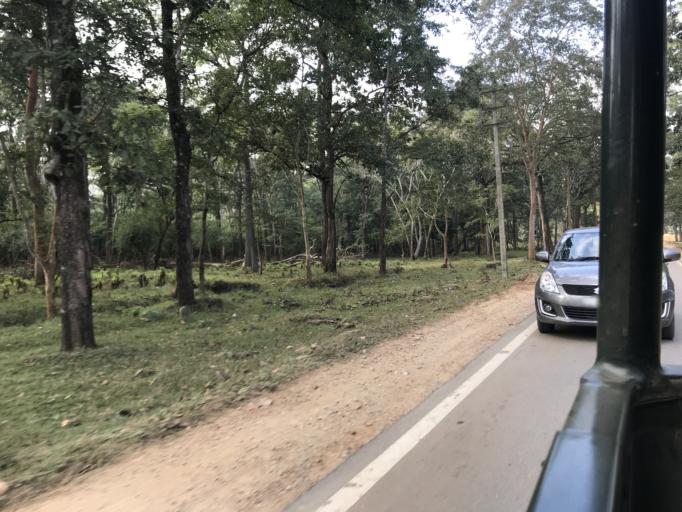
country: IN
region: Karnataka
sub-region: Mysore
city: Heggadadevankote
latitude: 11.9363
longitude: 76.1997
